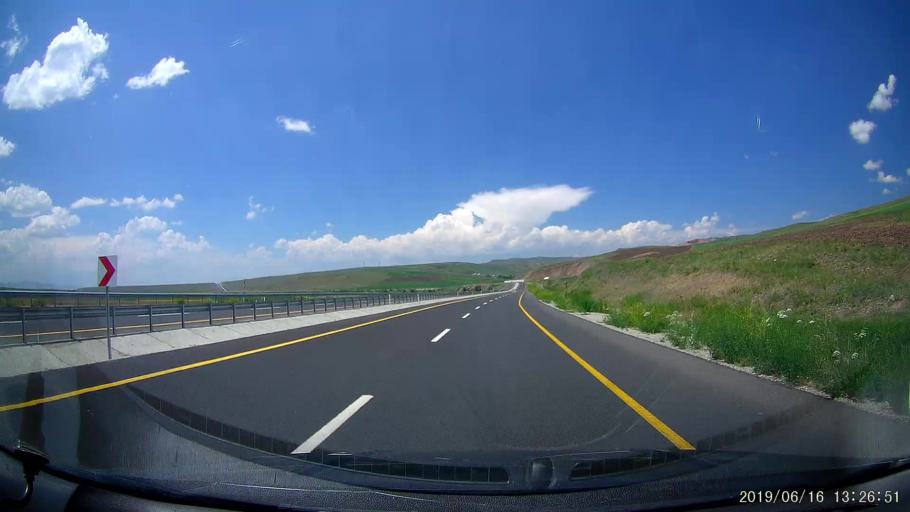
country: TR
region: Agri
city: Taslicay
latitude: 39.6628
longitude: 43.3194
